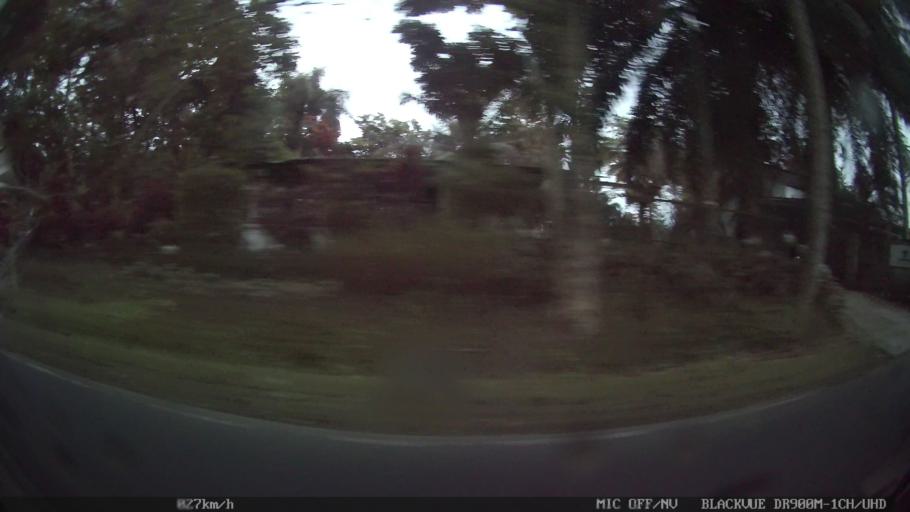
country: ID
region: Bali
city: Banjar Buahan
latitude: -8.4095
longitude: 115.2451
